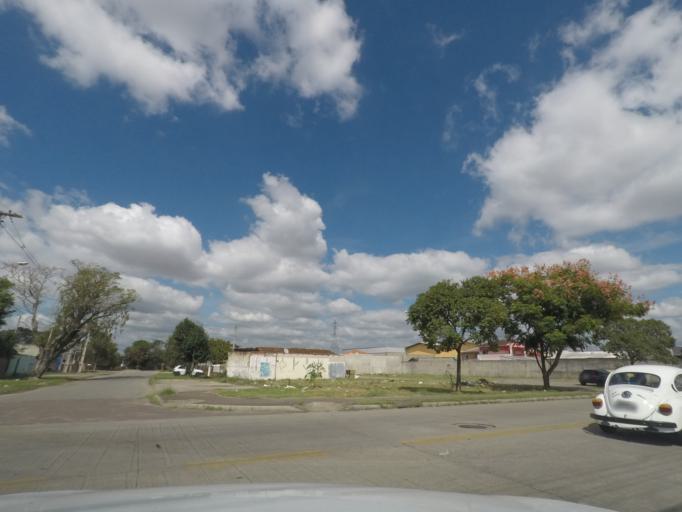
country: BR
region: Parana
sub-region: Sao Jose Dos Pinhais
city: Sao Jose dos Pinhais
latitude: -25.5078
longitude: -49.2160
